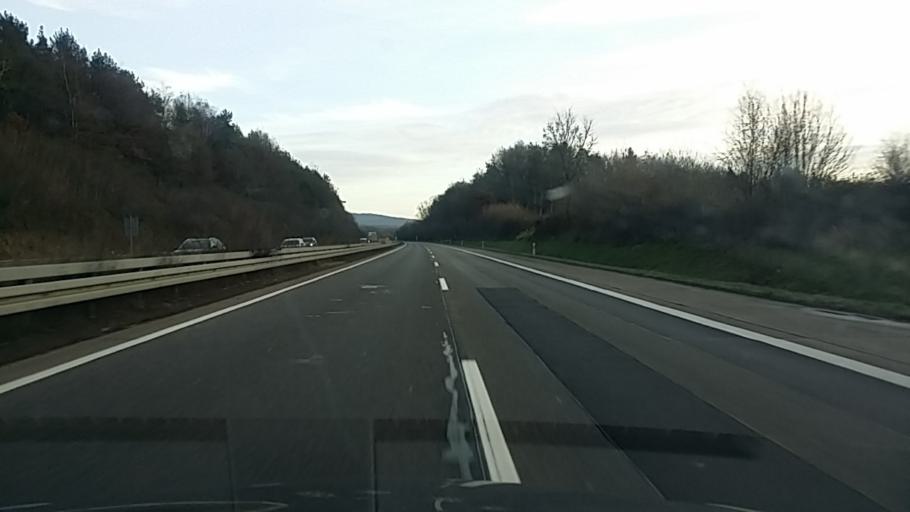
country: DE
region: Hesse
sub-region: Regierungsbezirk Kassel
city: Eichenzell
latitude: 50.4607
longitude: 9.7223
